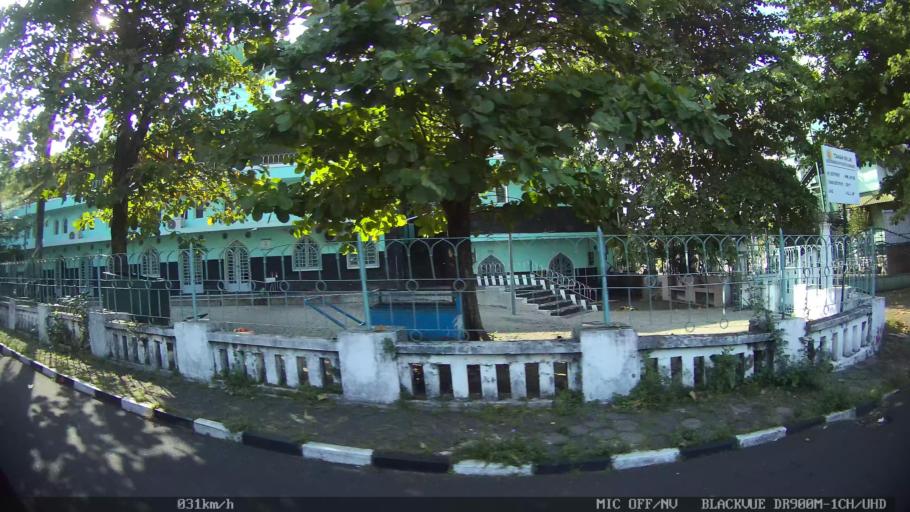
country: ID
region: Daerah Istimewa Yogyakarta
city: Yogyakarta
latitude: -7.7865
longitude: 110.3687
